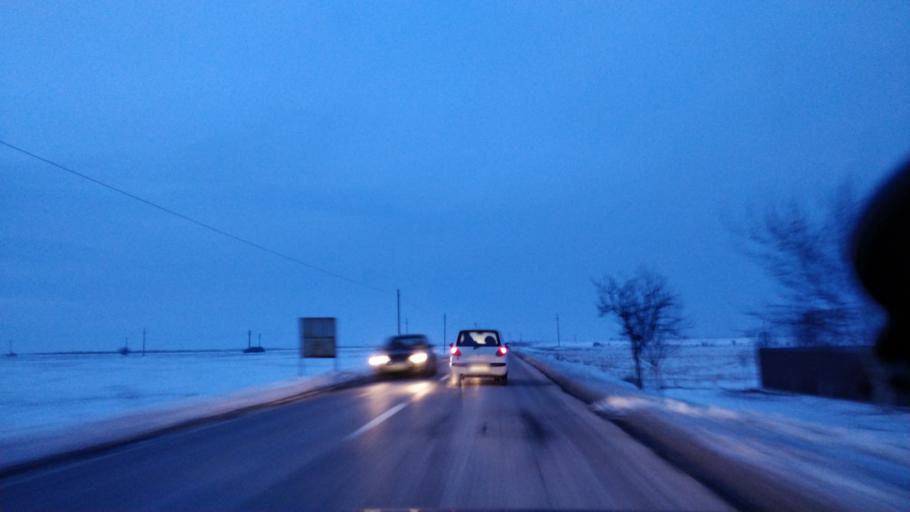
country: RO
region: Vrancea
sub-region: Comuna Nanesti
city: Nanesti
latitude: 45.5551
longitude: 27.5000
